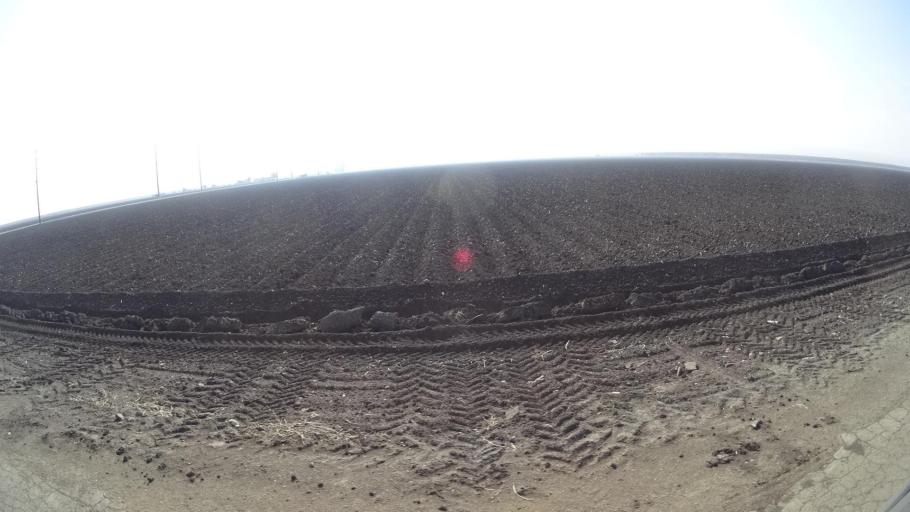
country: US
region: California
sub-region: Kern County
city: Buttonwillow
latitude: 35.3545
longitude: -119.4489
